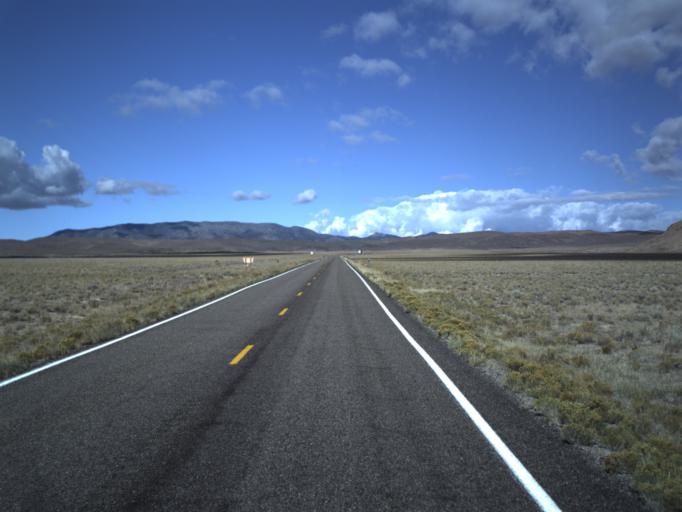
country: US
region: Utah
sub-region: Beaver County
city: Milford
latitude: 38.5722
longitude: -113.7899
